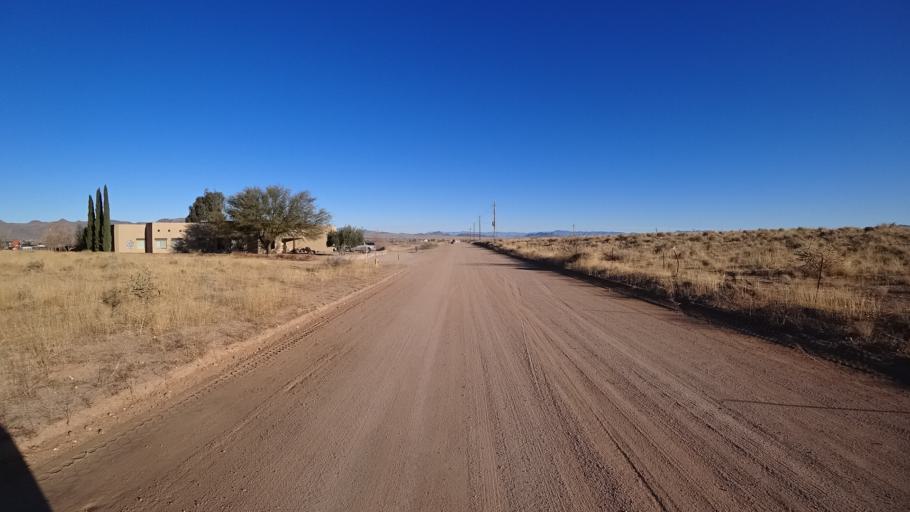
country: US
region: Arizona
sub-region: Mohave County
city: Kingman
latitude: 35.1975
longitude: -113.9940
